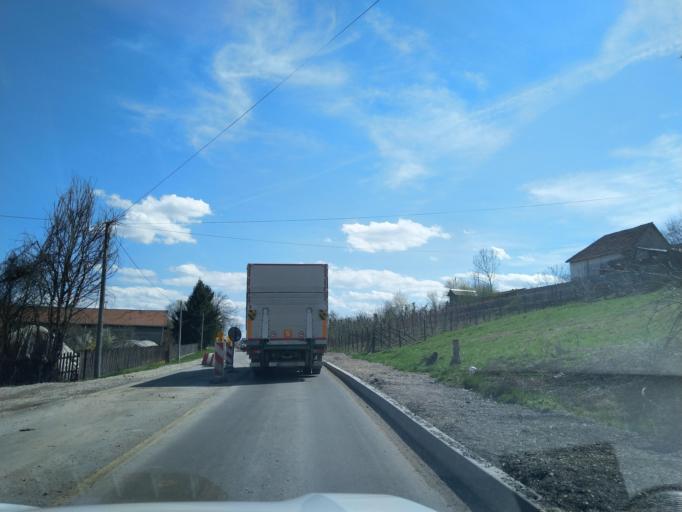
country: RS
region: Central Serbia
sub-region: Zlatiborski Okrug
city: Pozega
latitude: 43.8240
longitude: 20.0812
